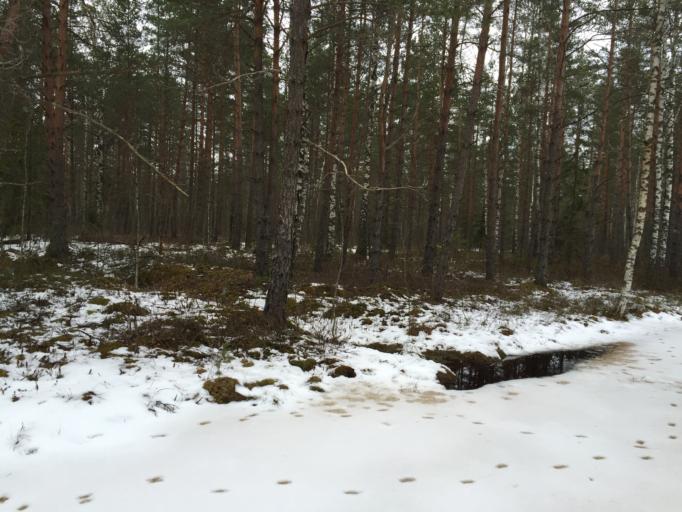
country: LV
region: Garkalne
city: Garkalne
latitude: 56.9601
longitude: 24.4632
